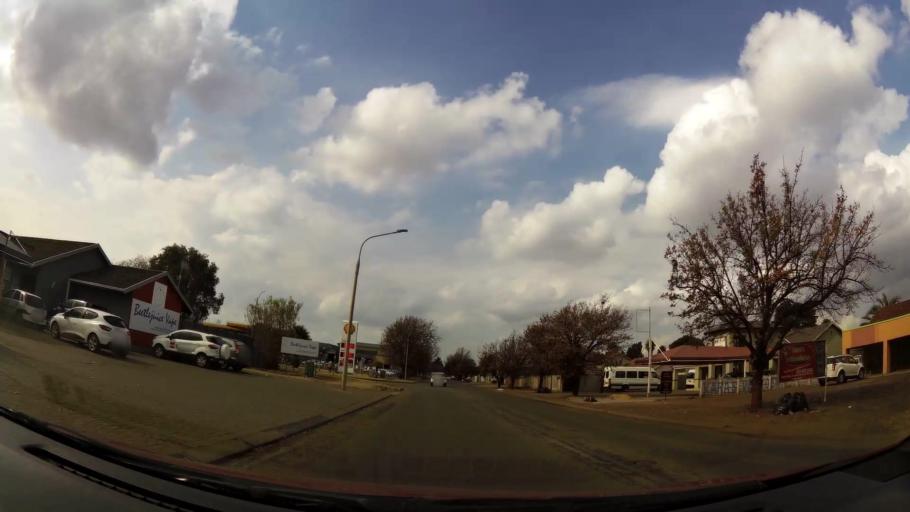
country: ZA
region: Gauteng
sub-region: Sedibeng District Municipality
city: Vanderbijlpark
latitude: -26.7245
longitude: 27.8543
